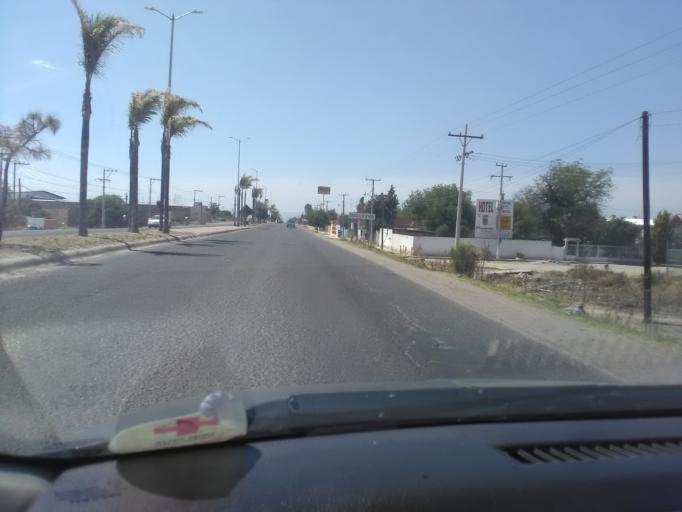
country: MX
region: Durango
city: Victoria de Durango
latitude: 24.0268
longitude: -104.5781
